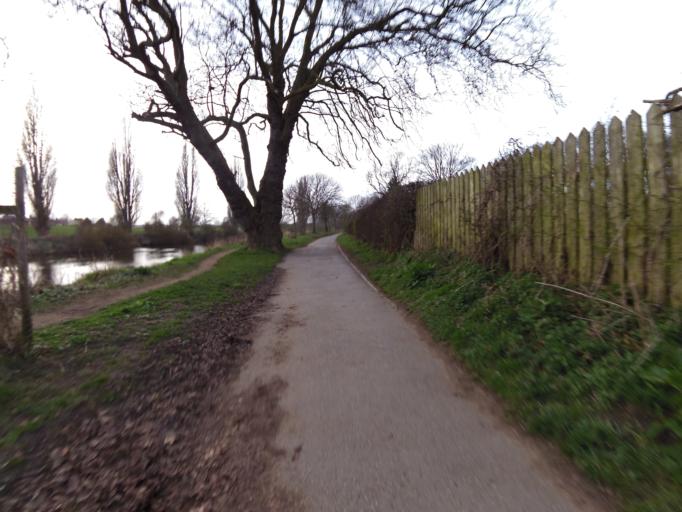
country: GB
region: England
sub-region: City of York
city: York
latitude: 53.9658
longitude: -1.1015
